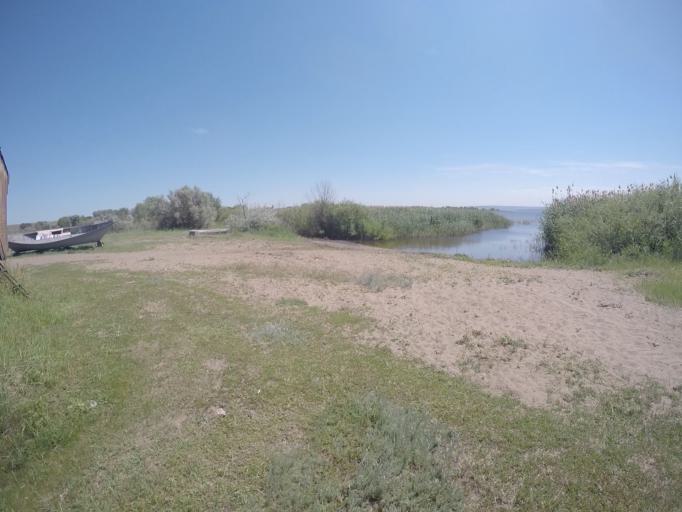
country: RU
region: Saratov
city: Krasnoarmeysk
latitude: 51.1501
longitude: 45.9198
